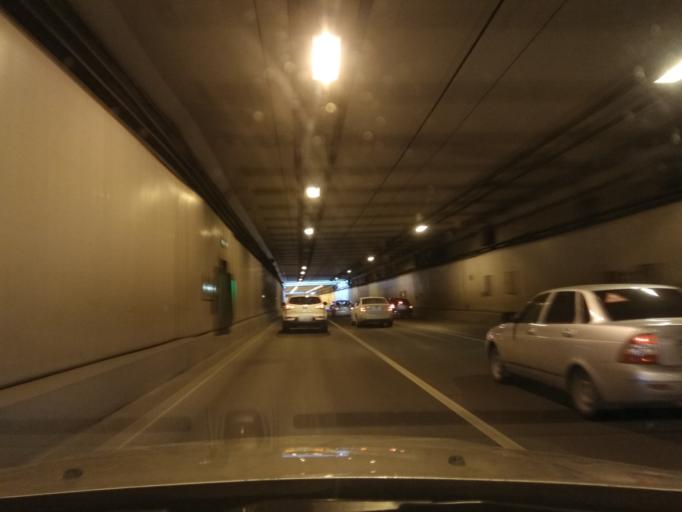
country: RU
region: Moskovskaya
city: Koptevo
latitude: 55.8143
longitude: 37.5184
